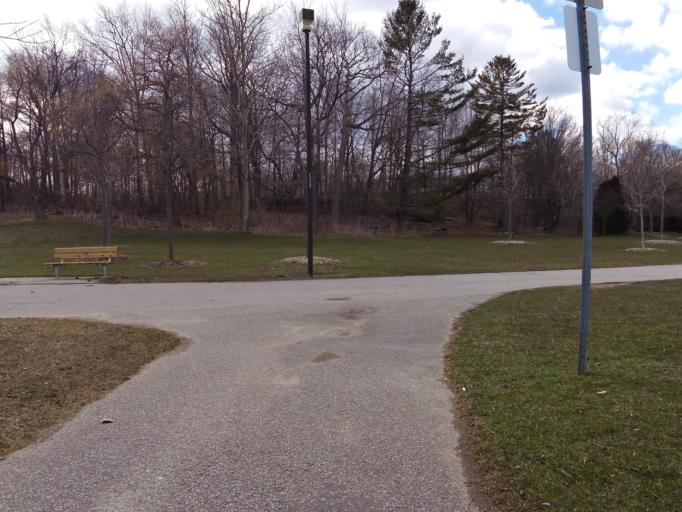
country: CA
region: Ontario
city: Mississauga
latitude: 43.5244
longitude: -79.6020
